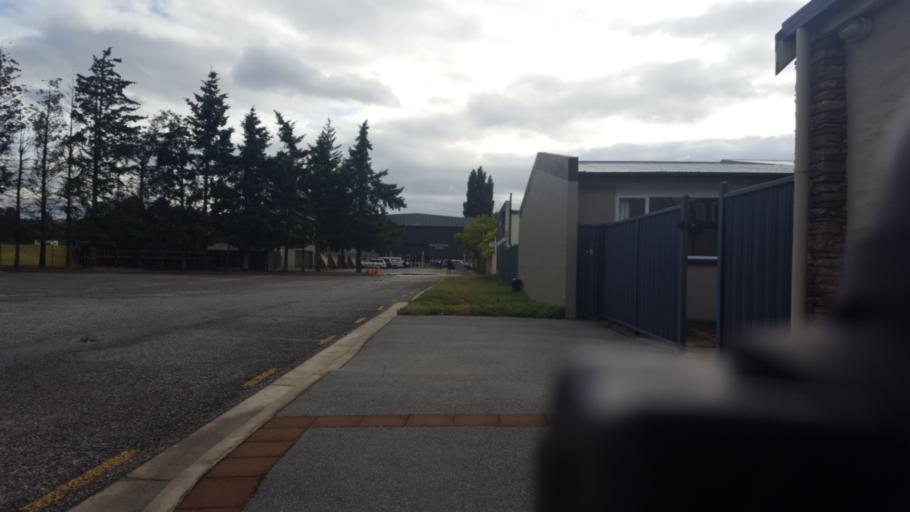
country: NZ
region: Otago
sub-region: Queenstown-Lakes District
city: Wanaka
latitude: -45.2449
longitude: 169.3828
